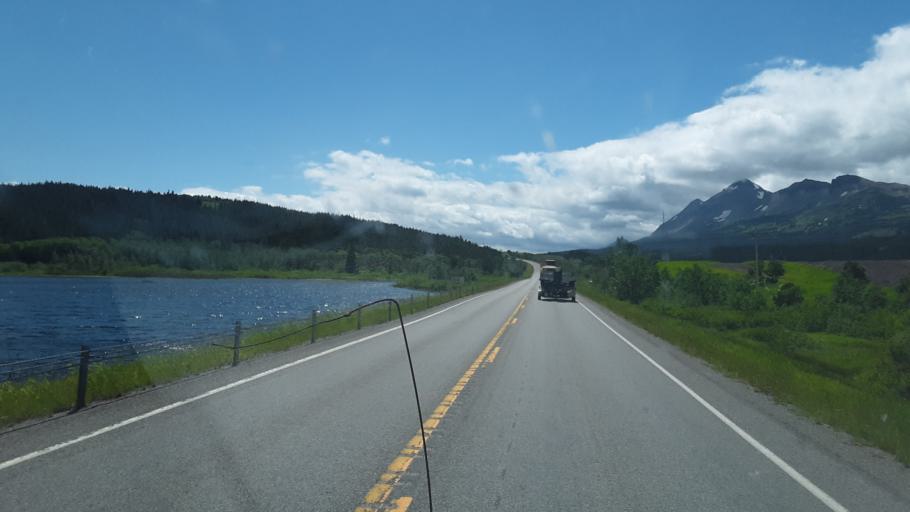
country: US
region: Montana
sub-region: Glacier County
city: South Browning
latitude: 48.3877
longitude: -113.2639
